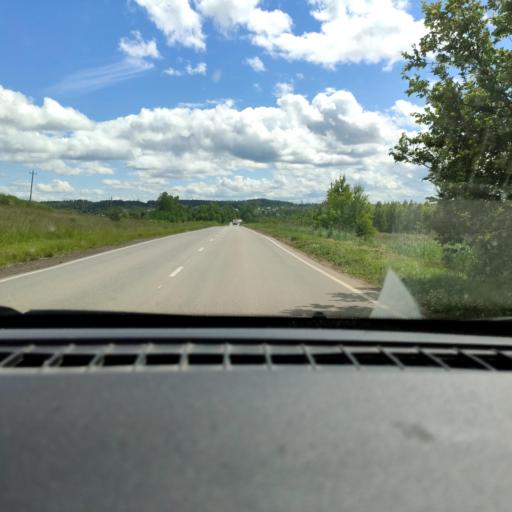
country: RU
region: Perm
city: Overyata
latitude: 58.1212
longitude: 55.8173
